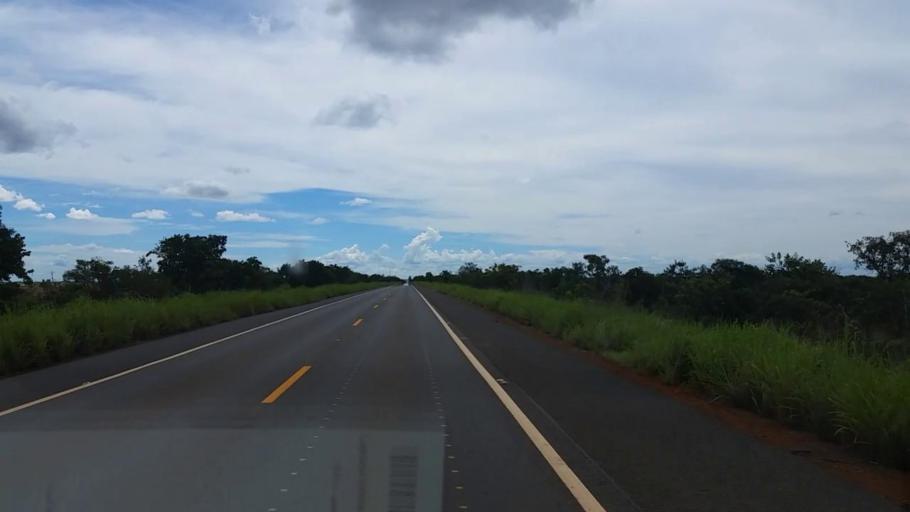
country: BR
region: Goias
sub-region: Luziania
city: Luziania
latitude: -16.2088
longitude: -47.4222
